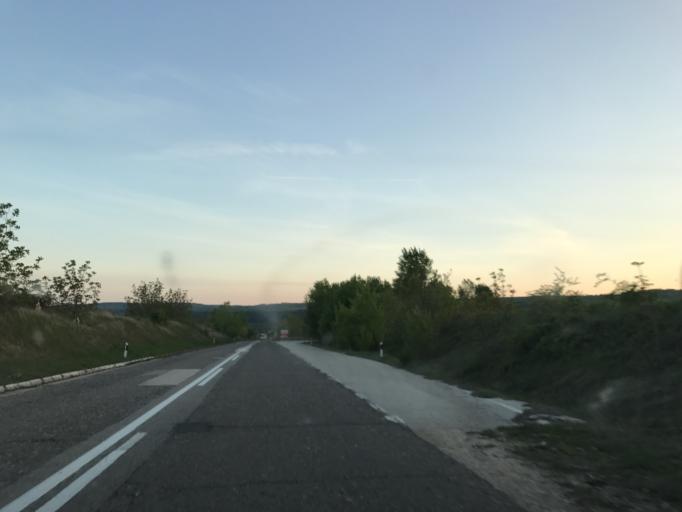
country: RS
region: Central Serbia
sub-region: Borski Okrug
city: Negotin
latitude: 44.2405
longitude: 22.5156
